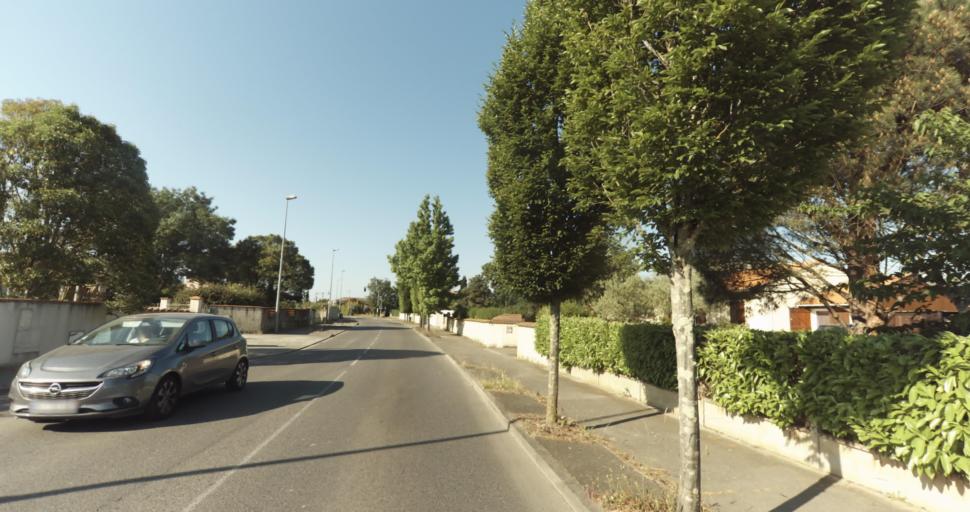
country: FR
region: Midi-Pyrenees
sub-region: Departement de la Haute-Garonne
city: La Salvetat-Saint-Gilles
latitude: 43.5689
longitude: 1.2668
